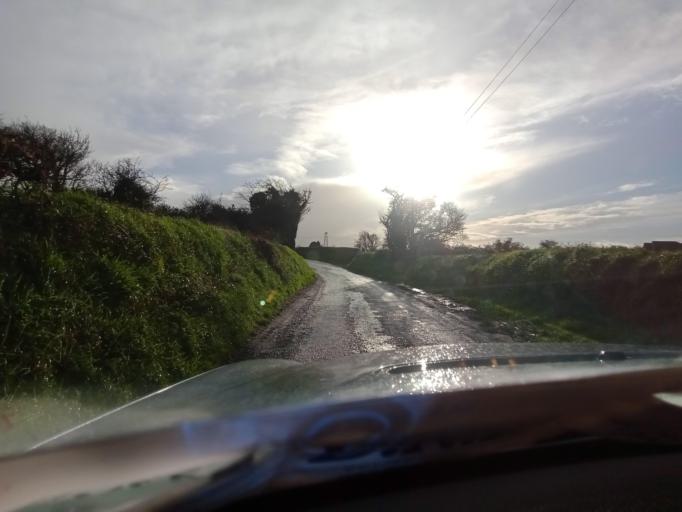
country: IE
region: Leinster
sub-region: Kilkenny
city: Mooncoin
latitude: 52.2810
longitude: -7.1980
